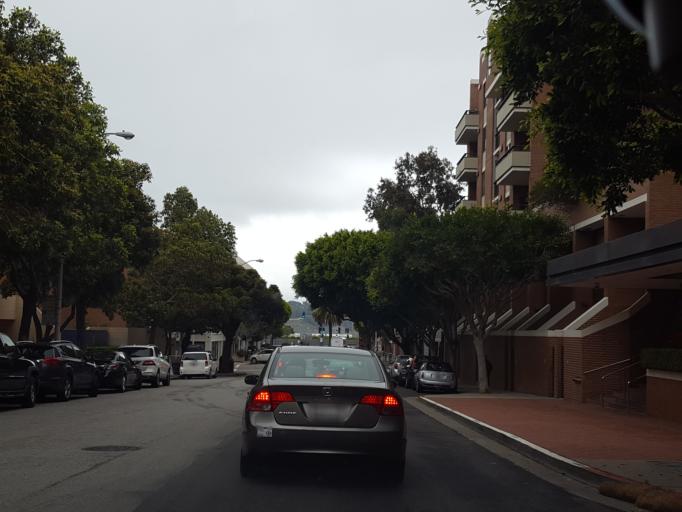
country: US
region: California
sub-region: San Francisco County
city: San Francisco
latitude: 37.8039
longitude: -122.4044
